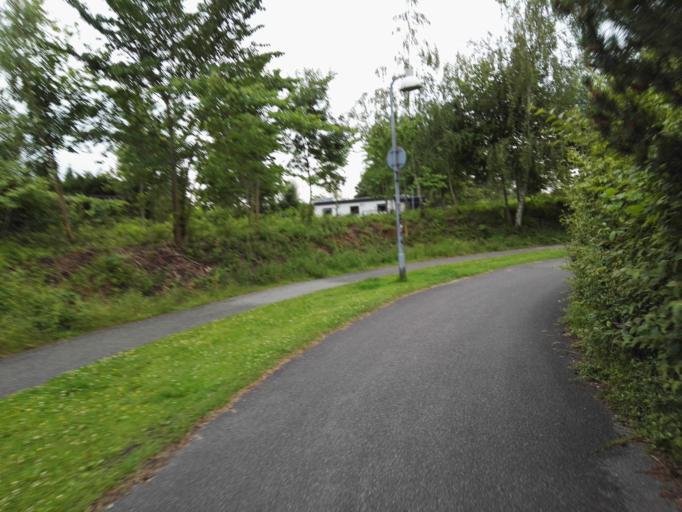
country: DK
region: Capital Region
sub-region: Egedal Kommune
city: Smorumnedre
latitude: 55.7417
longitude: 12.3005
